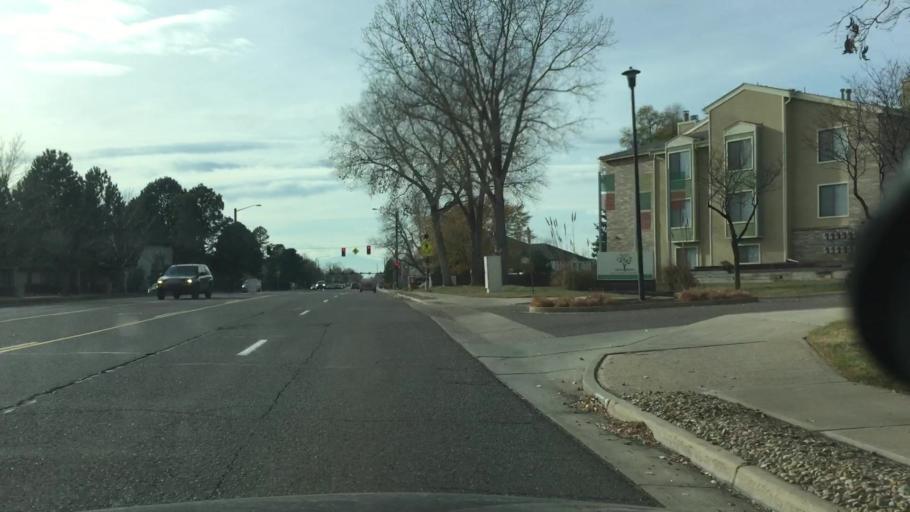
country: US
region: Colorado
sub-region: Arapahoe County
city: Glendale
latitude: 39.6894
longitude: -104.8837
